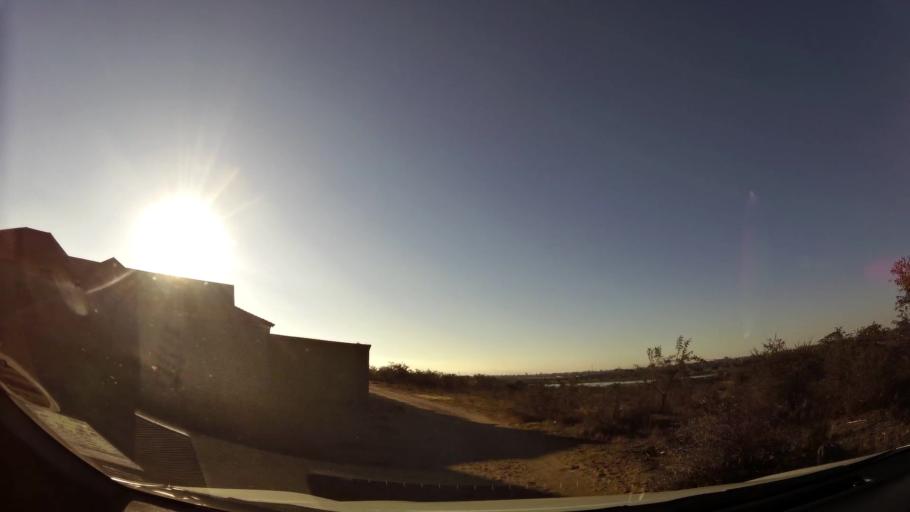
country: ZA
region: Limpopo
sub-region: Capricorn District Municipality
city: Polokwane
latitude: -23.8414
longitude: 29.3631
